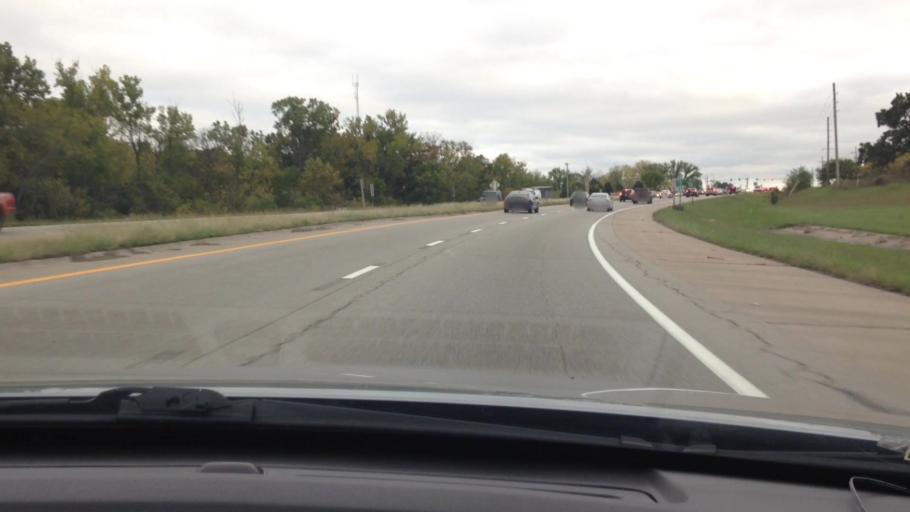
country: US
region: Kansas
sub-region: Wyandotte County
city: Bonner Springs
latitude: 39.1038
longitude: -94.8821
